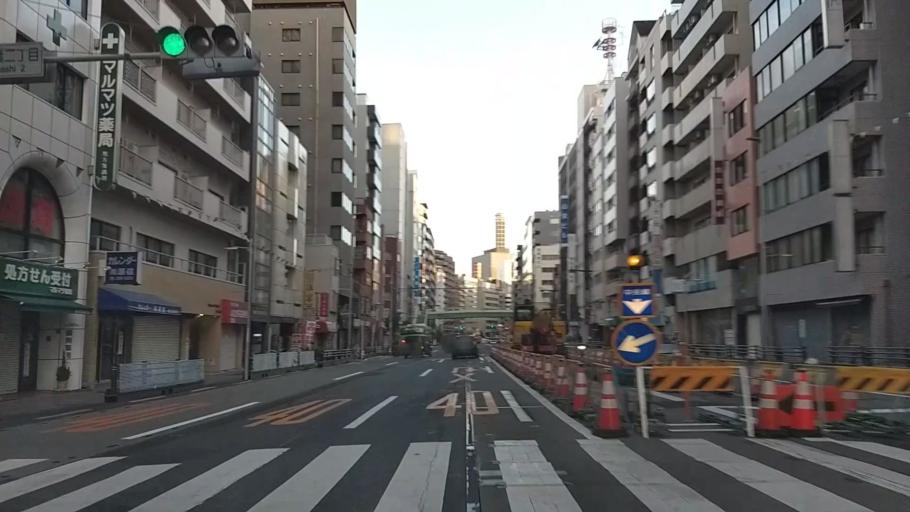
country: JP
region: Tokyo
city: Tokyo
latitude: 35.7002
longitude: 139.7481
